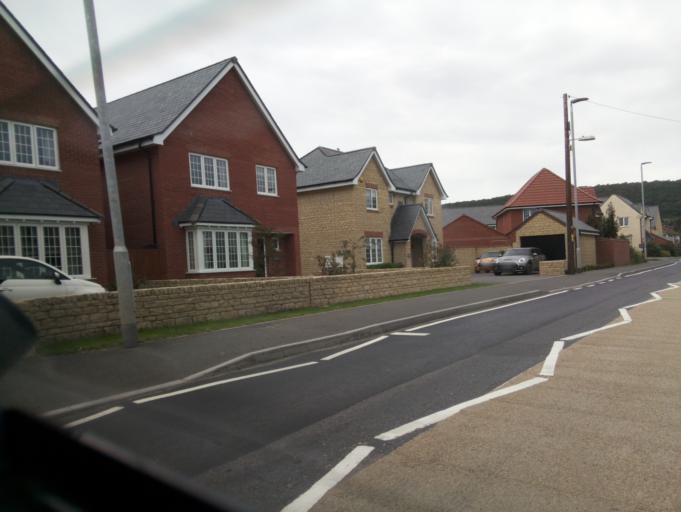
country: GB
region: England
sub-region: Somerset
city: Cheddar
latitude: 51.2807
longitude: -2.7891
